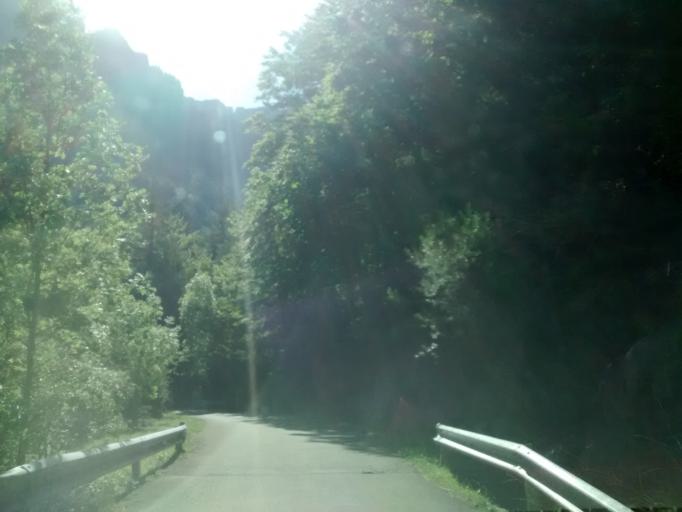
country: ES
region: Aragon
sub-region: Provincia de Huesca
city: Aragues del Puerto
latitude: 42.8143
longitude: -0.7131
